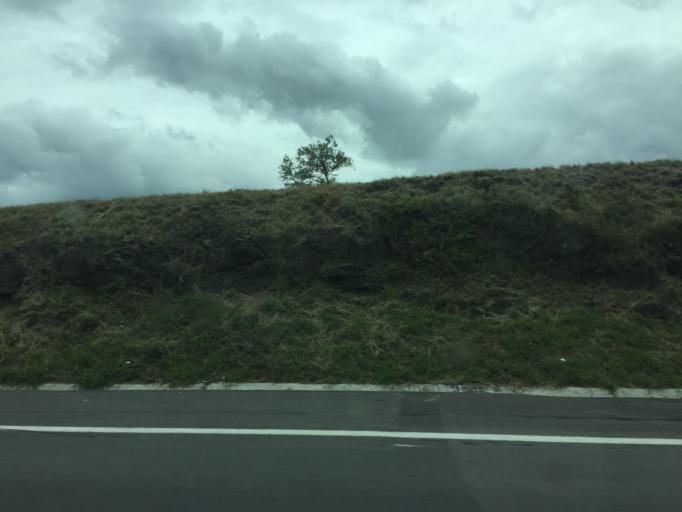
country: MX
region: Jalisco
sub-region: Tonala
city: Mismaloya (Fraccionamiento Pedregal de Santa Martha)
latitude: 20.6032
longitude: -103.1426
